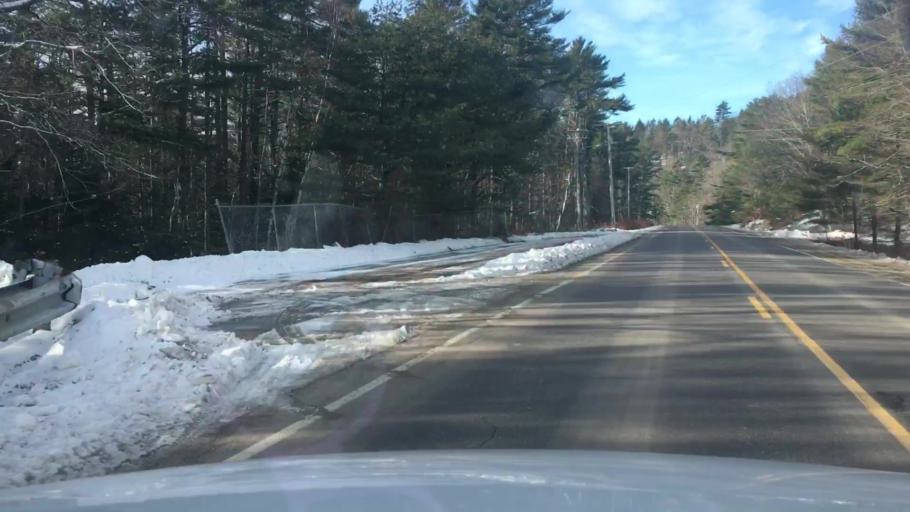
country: US
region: Maine
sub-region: Lincoln County
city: Wiscasset
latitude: 43.9732
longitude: -69.6756
